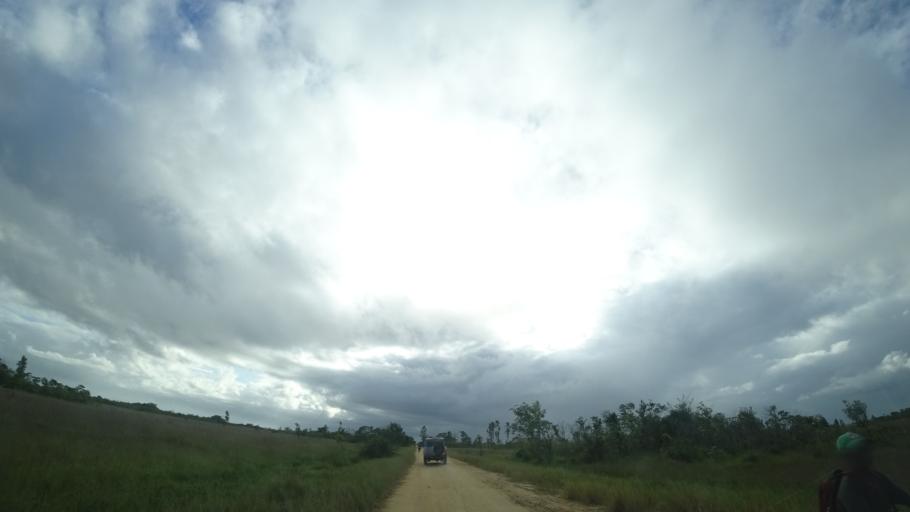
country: MZ
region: Sofala
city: Beira
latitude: -19.6929
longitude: 35.0383
